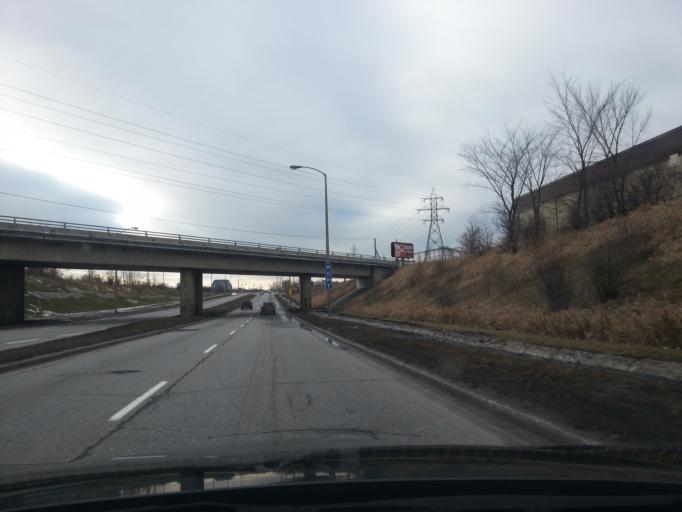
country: CA
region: Ontario
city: Ottawa
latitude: 45.4121
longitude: -75.6153
